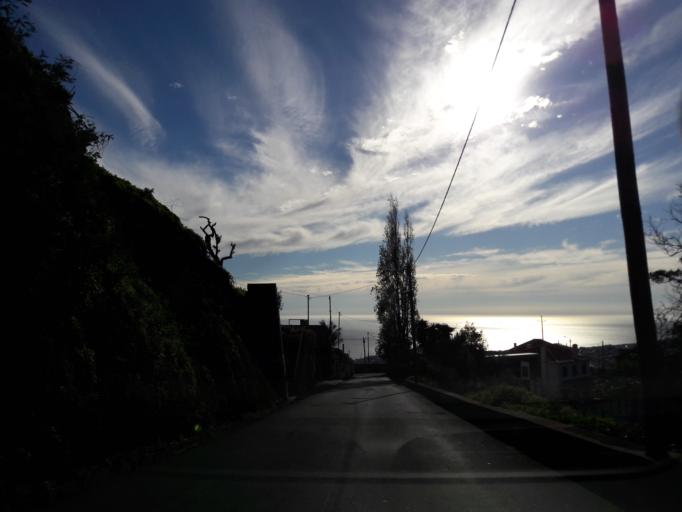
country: PT
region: Madeira
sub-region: Funchal
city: Nossa Senhora do Monte
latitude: 32.6749
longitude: -16.9106
